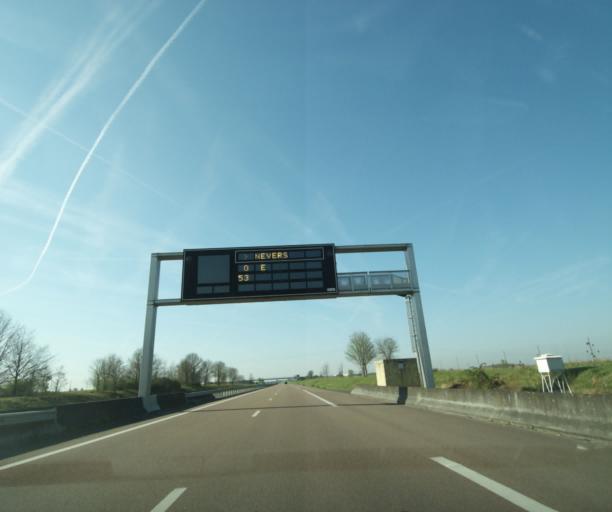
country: FR
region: Ile-de-France
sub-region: Departement de Seine-et-Marne
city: Souppes-sur-Loing
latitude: 48.2015
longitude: 2.7712
